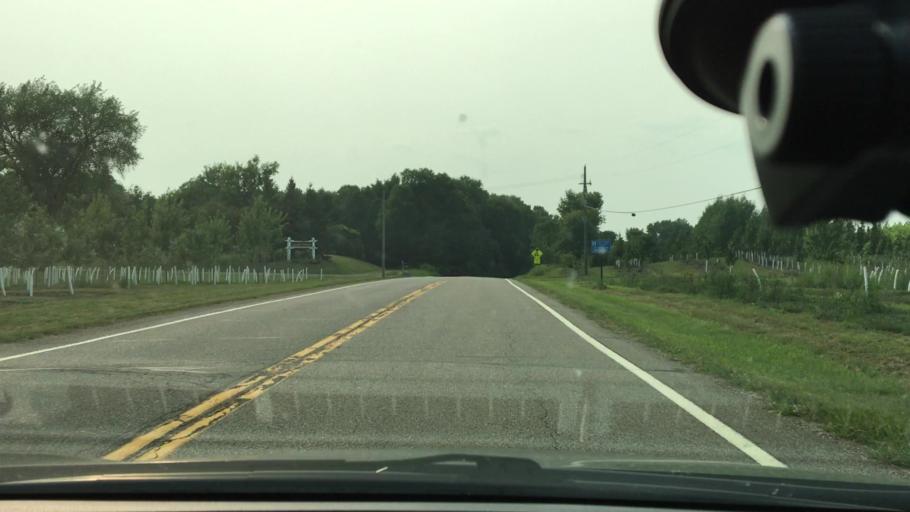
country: US
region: Minnesota
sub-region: Hennepin County
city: Dayton
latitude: 45.2236
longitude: -93.4837
